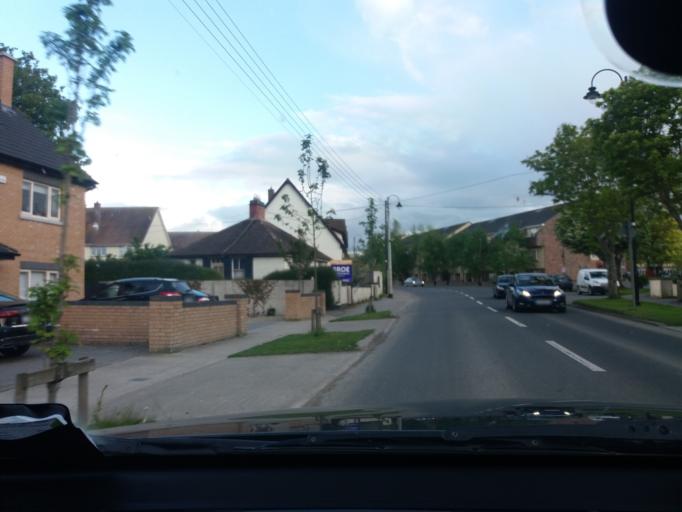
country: IE
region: Leinster
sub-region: South Dublin
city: Newcastle
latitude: 53.2975
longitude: -6.4935
